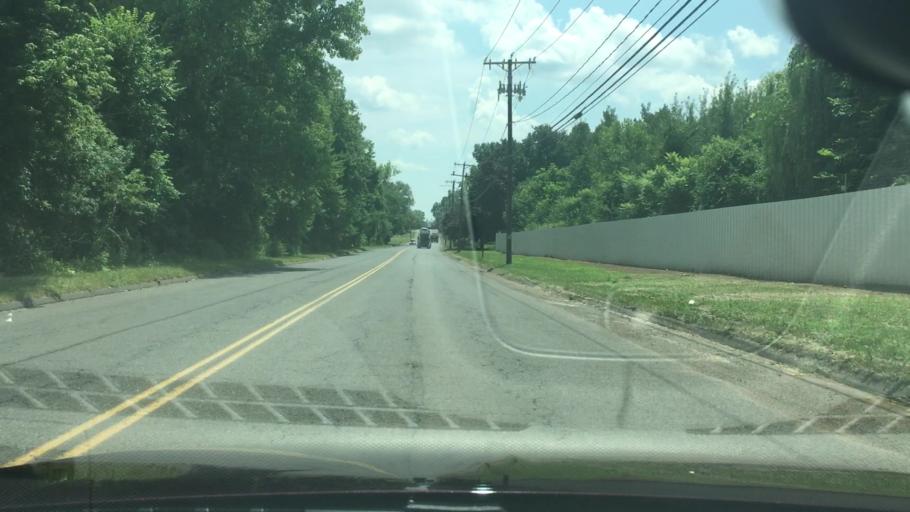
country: US
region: Connecticut
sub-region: Hartford County
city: Kensington
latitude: 41.6441
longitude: -72.7508
